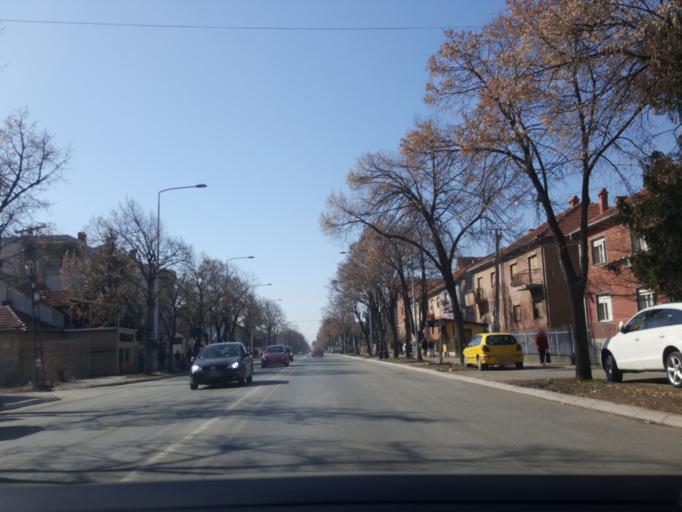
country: RS
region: Central Serbia
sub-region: Nisavski Okrug
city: Nis
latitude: 43.3294
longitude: 21.9212
